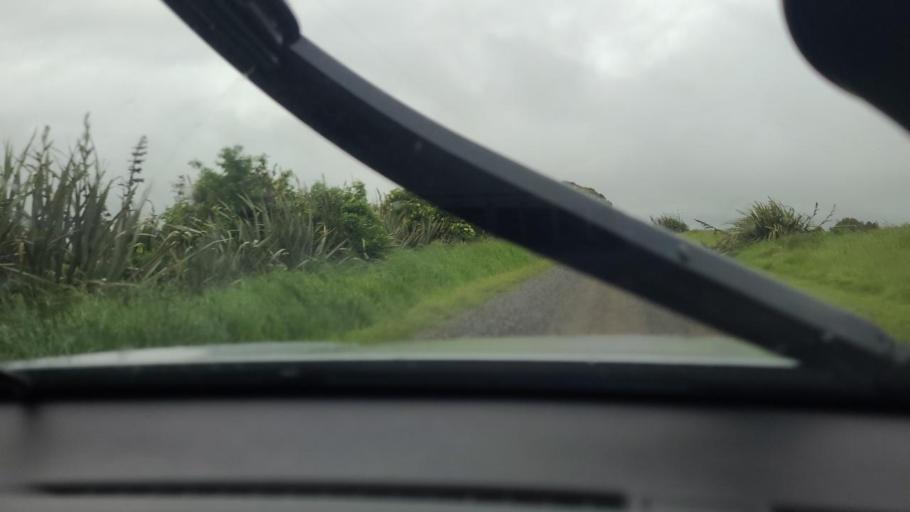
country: NZ
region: Southland
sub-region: Southland District
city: Riverton
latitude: -46.1917
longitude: 168.0345
